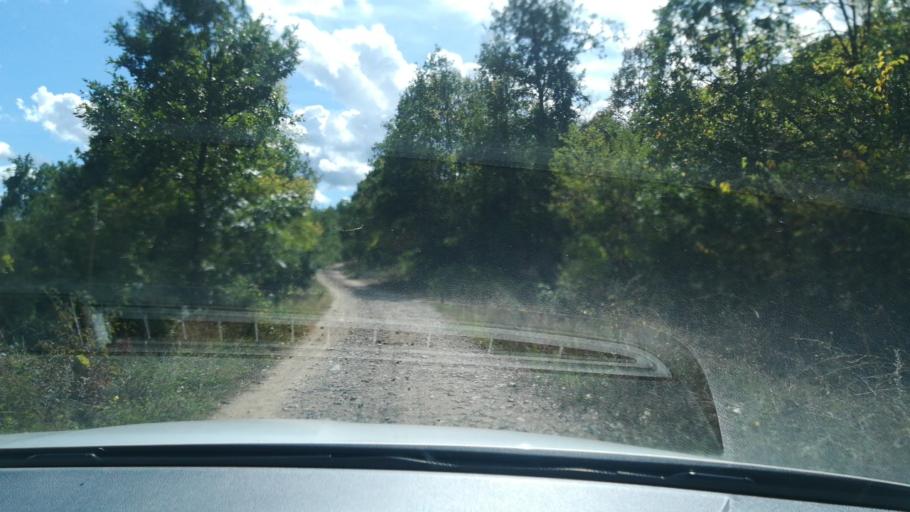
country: MK
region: Delcevo
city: Delcevo
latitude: 41.8996
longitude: 22.8054
